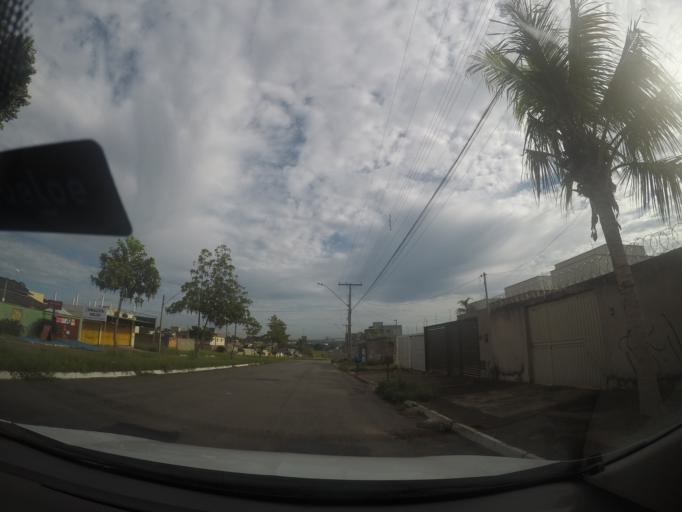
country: BR
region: Goias
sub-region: Goiania
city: Goiania
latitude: -16.6797
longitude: -49.2022
